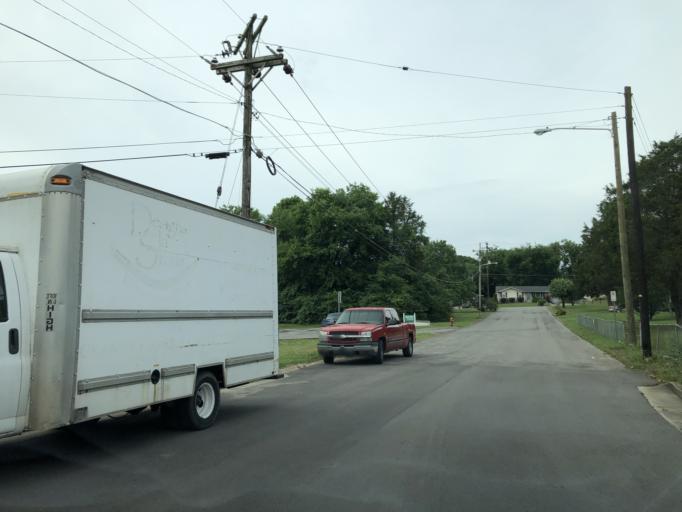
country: US
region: Tennessee
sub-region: Davidson County
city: Goodlettsville
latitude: 36.2799
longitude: -86.6965
